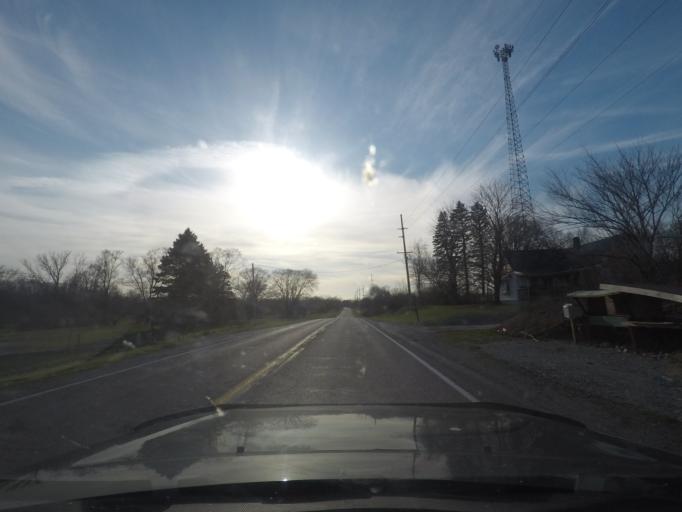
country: US
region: Indiana
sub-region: Saint Joseph County
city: Walkerton
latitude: 41.4513
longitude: -86.4504
